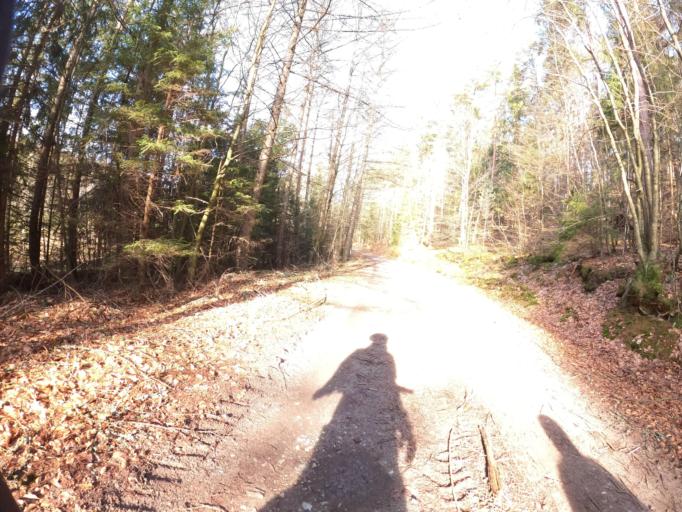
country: PL
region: West Pomeranian Voivodeship
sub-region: Powiat koszalinski
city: Polanow
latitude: 54.2338
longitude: 16.6772
